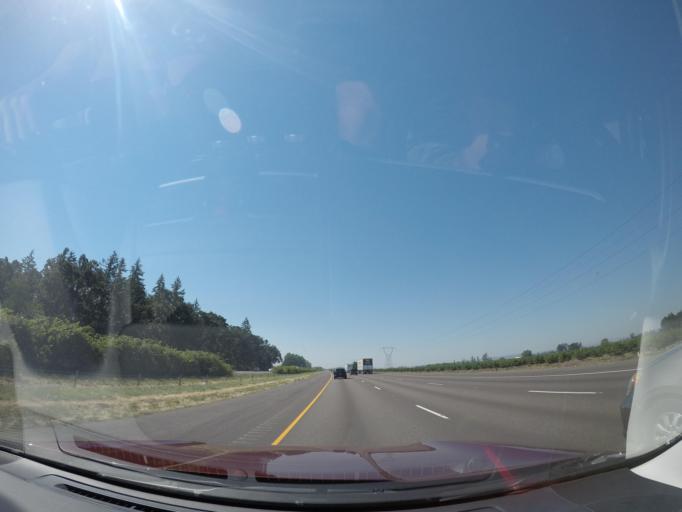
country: US
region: Oregon
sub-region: Marion County
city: Gervais
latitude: 45.0719
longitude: -122.9609
